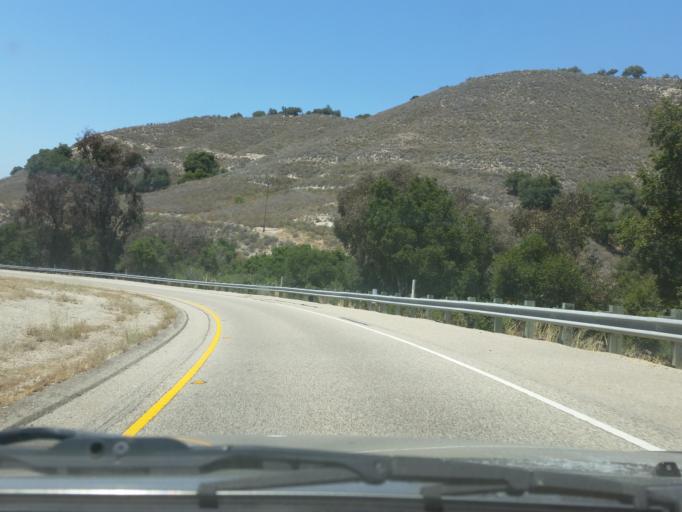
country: US
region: California
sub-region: San Luis Obispo County
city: Avila Beach
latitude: 35.1788
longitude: -120.6975
